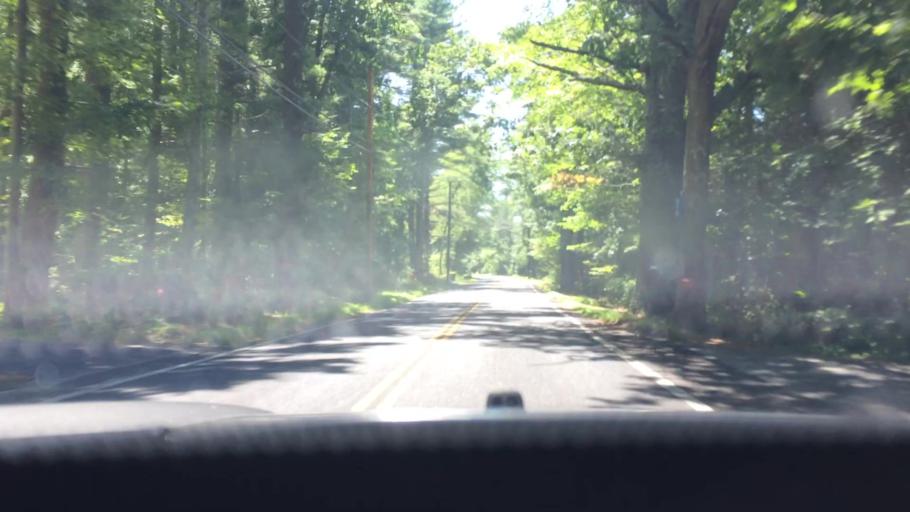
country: US
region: Rhode Island
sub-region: Providence County
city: Harrisville
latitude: 41.9829
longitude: -71.6831
